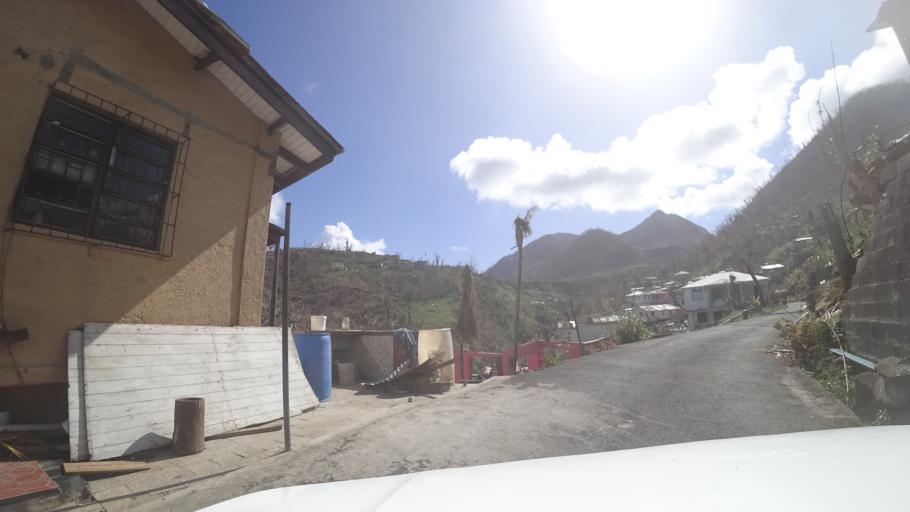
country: DM
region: Saint Patrick
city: Berekua
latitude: 15.2404
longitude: -61.3215
